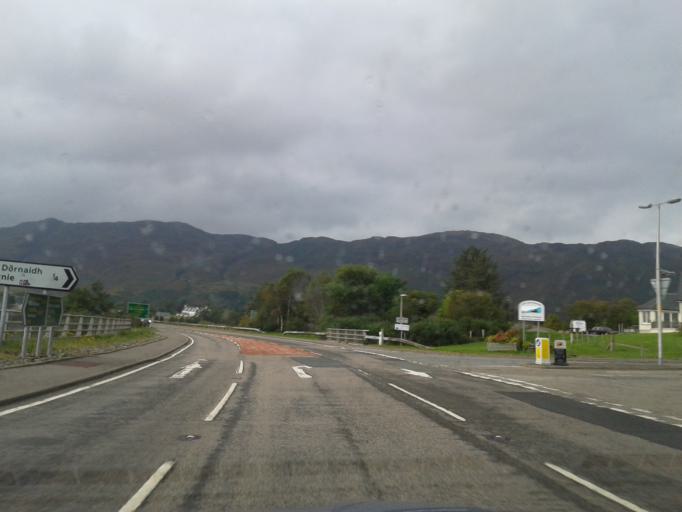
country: GB
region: Scotland
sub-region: Highland
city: Fort William
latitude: 57.2762
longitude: -5.5139
